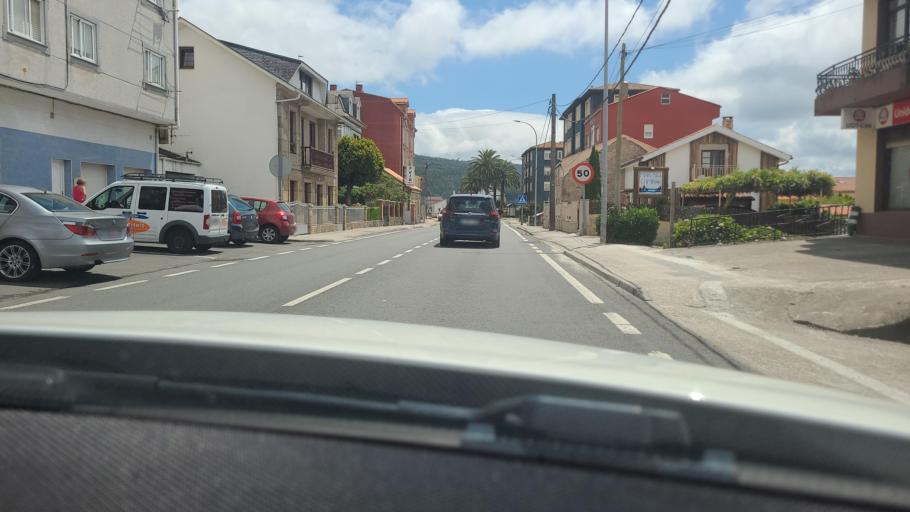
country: ES
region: Galicia
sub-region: Provincia da Coruna
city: Cee
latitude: 42.9490
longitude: -9.1828
